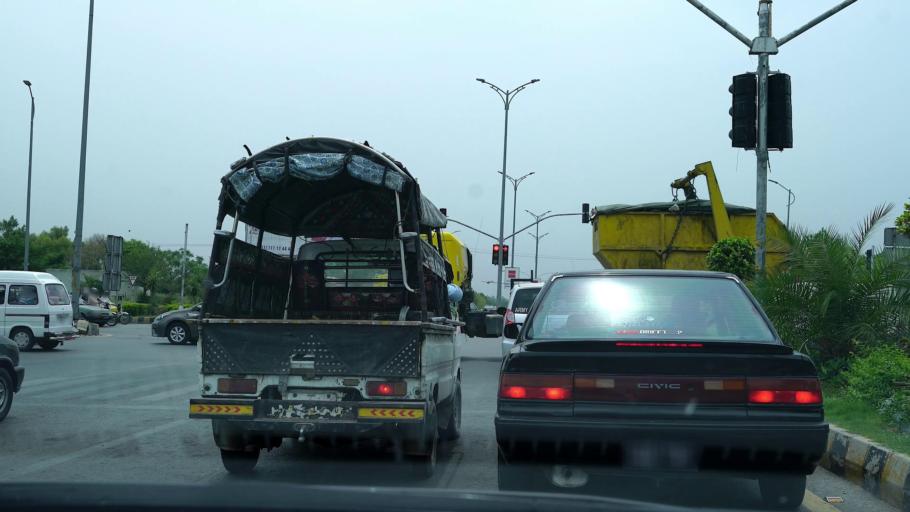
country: PK
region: Islamabad
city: Islamabad
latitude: 33.7031
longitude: 73.0441
